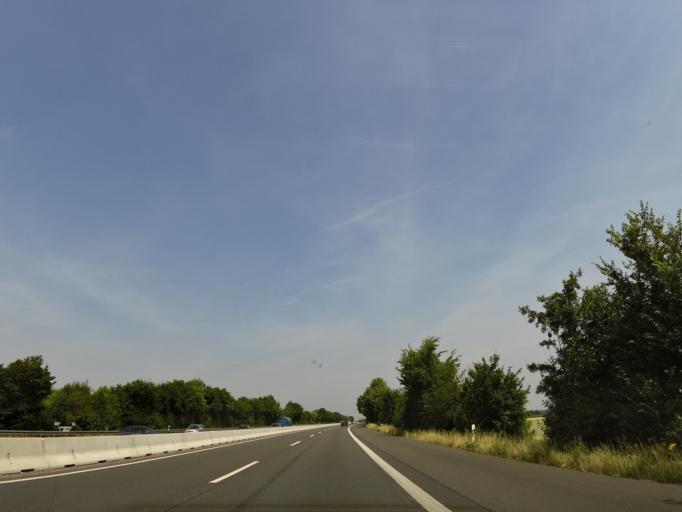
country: DE
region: North Rhine-Westphalia
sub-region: Regierungsbezirk Koln
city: Rheinbach
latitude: 50.6602
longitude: 6.9243
